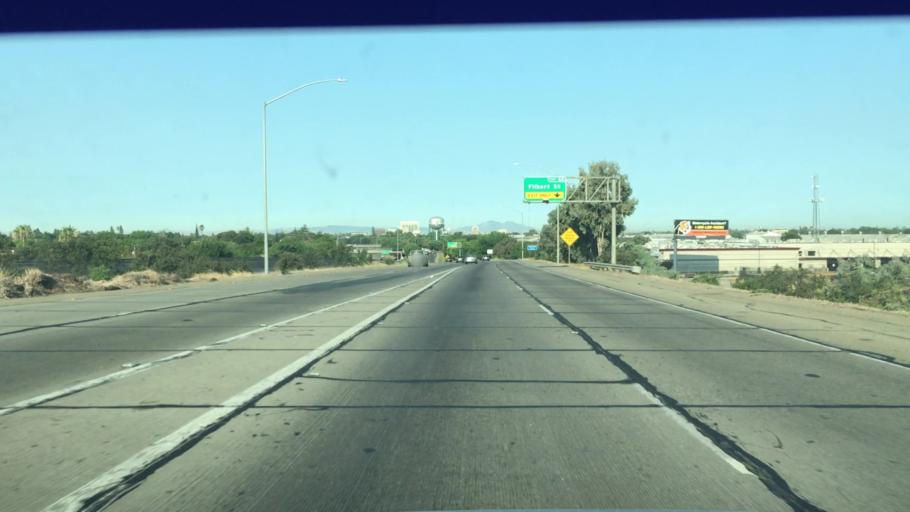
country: US
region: California
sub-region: San Joaquin County
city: Garden Acres
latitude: 37.9615
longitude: -121.2458
